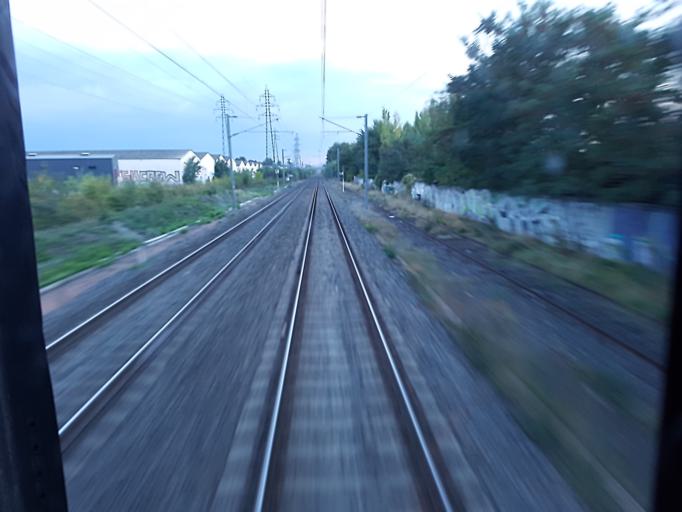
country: FR
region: Auvergne
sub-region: Departement du Puy-de-Dome
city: Menetrol
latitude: 45.8821
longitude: 3.1229
